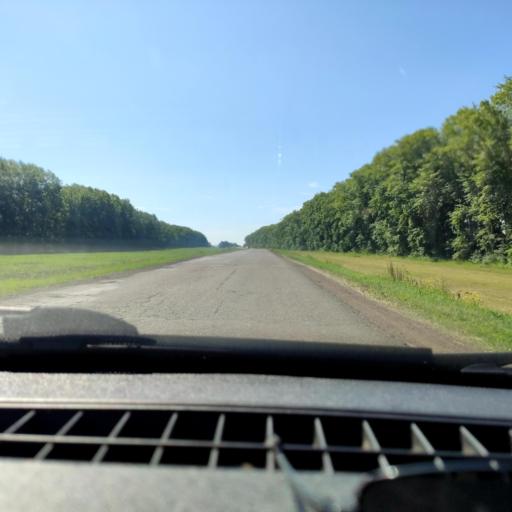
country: RU
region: Bashkortostan
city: Karmaskaly
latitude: 54.3943
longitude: 56.1709
